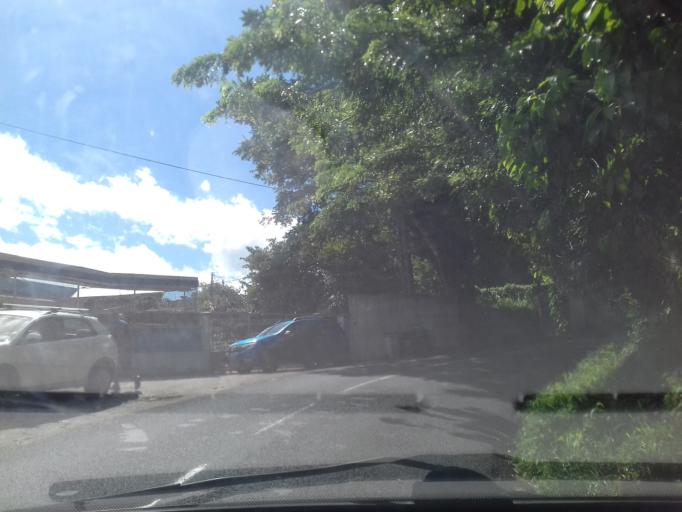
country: MQ
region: Martinique
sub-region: Martinique
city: Saint-Joseph
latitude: 14.6421
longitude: -61.0531
